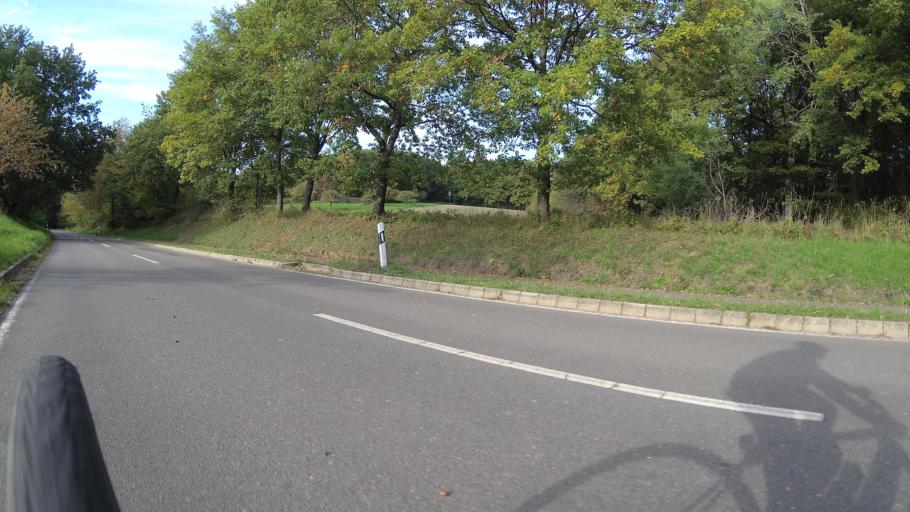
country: DE
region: Rheinland-Pfalz
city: Borsborn
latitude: 49.4469
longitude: 7.3878
